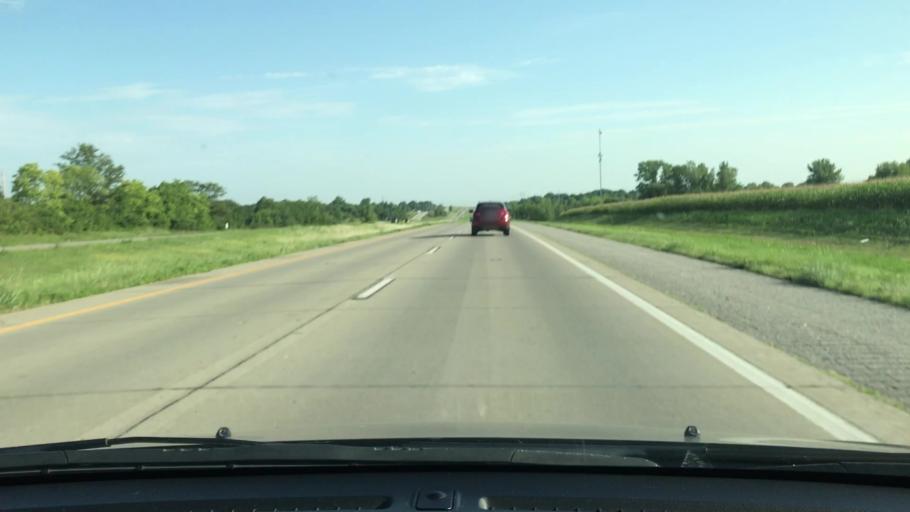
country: US
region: Missouri
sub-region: Jackson County
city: Lees Summit
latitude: 38.8744
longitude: -94.3748
